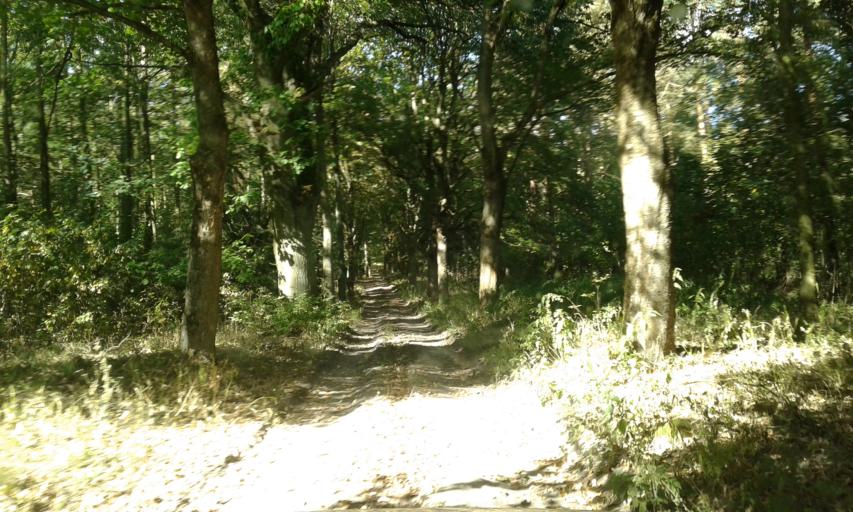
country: PL
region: West Pomeranian Voivodeship
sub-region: Powiat stargardzki
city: Dolice
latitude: 53.2384
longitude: 15.2544
